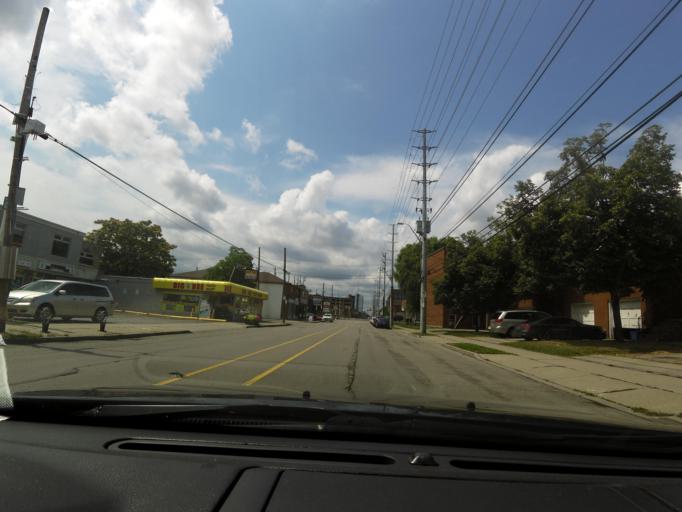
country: CA
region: Ontario
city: Hamilton
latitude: 43.2385
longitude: -79.8420
